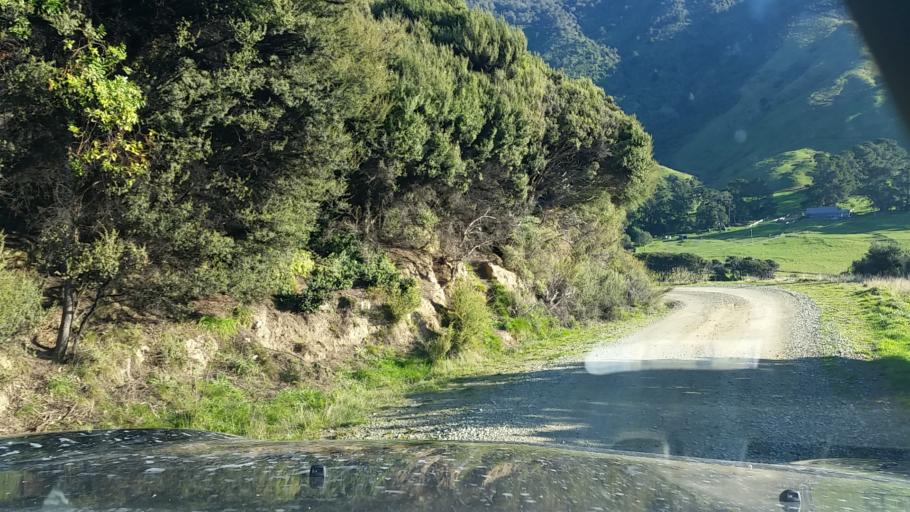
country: NZ
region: Marlborough
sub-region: Marlborough District
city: Picton
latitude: -41.0194
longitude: 174.1392
